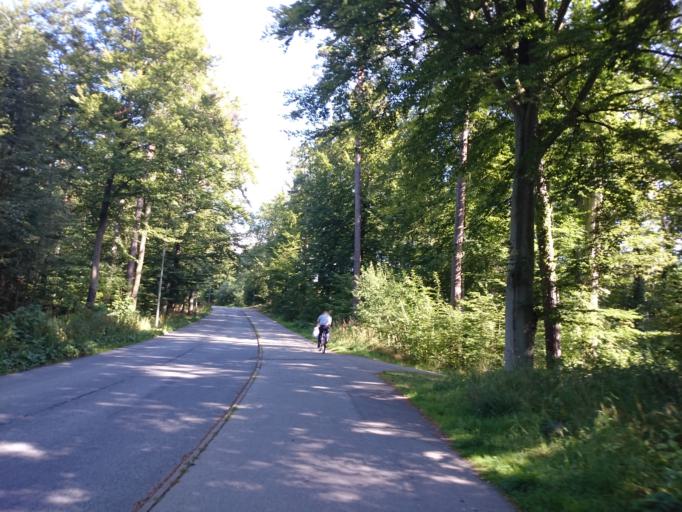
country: SE
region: Blekinge
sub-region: Karlshamns Kommun
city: Karlshamn
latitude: 56.1633
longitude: 14.8771
